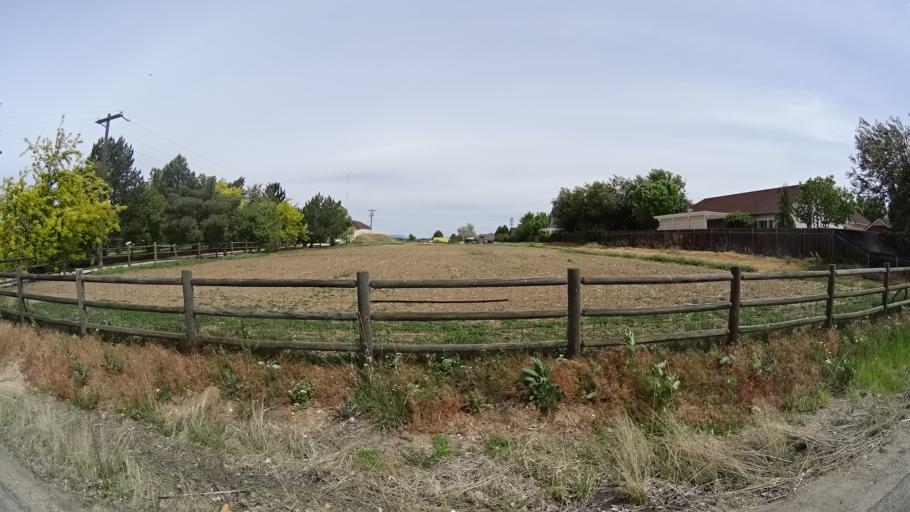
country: US
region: Idaho
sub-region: Ada County
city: Meridian
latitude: 43.5612
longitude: -116.3366
